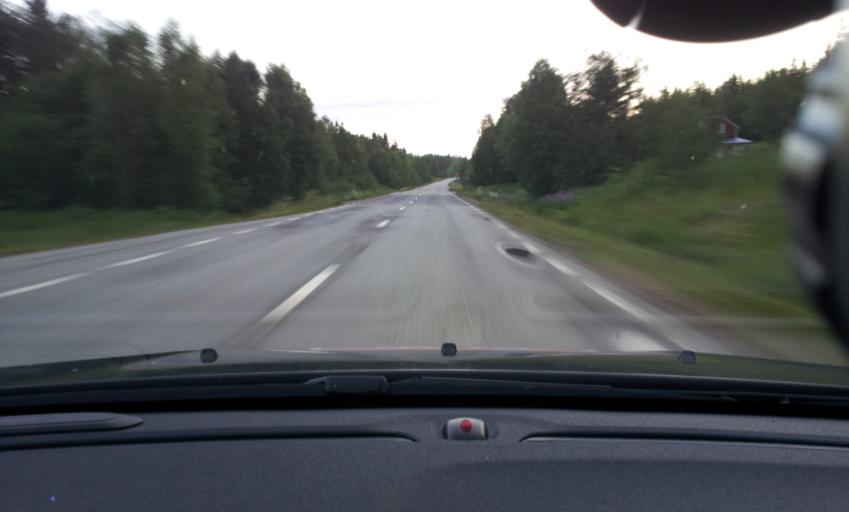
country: SE
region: Jaemtland
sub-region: Ragunda Kommun
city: Hammarstrand
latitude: 63.0271
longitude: 16.3056
